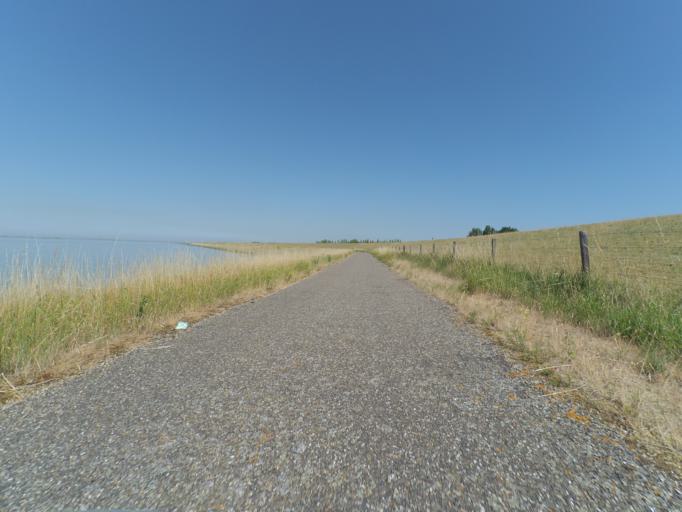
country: NL
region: Zeeland
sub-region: Gemeente Reimerswaal
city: Yerseke
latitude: 51.3984
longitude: 4.1361
